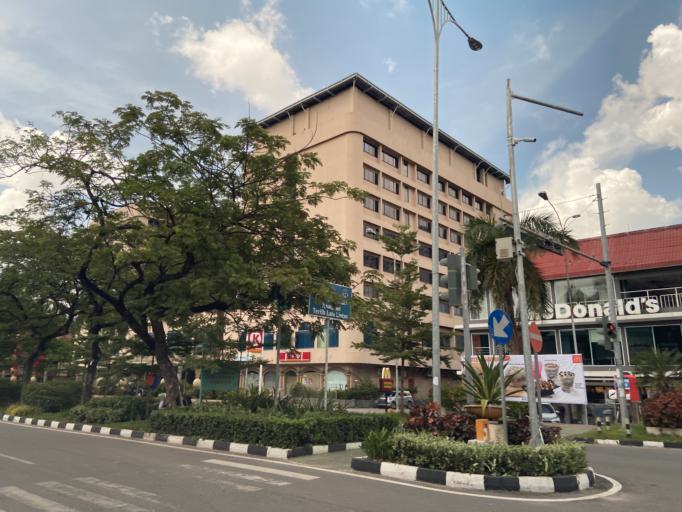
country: SG
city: Singapore
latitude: 1.1504
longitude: 104.0071
